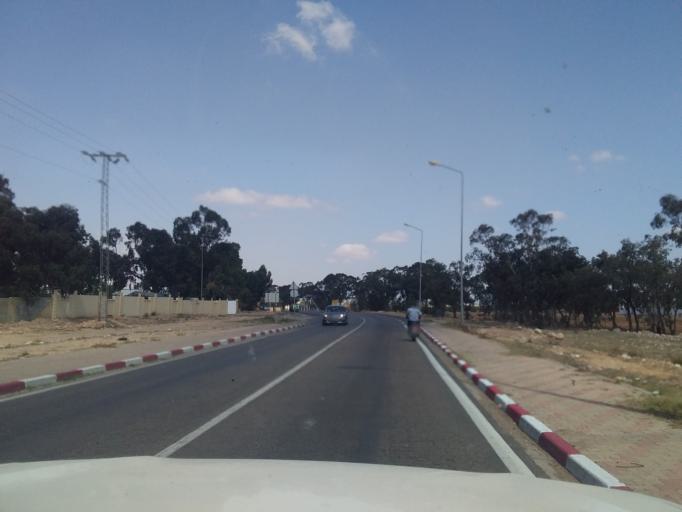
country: TN
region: Madanin
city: Medenine
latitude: 33.5997
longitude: 10.3091
